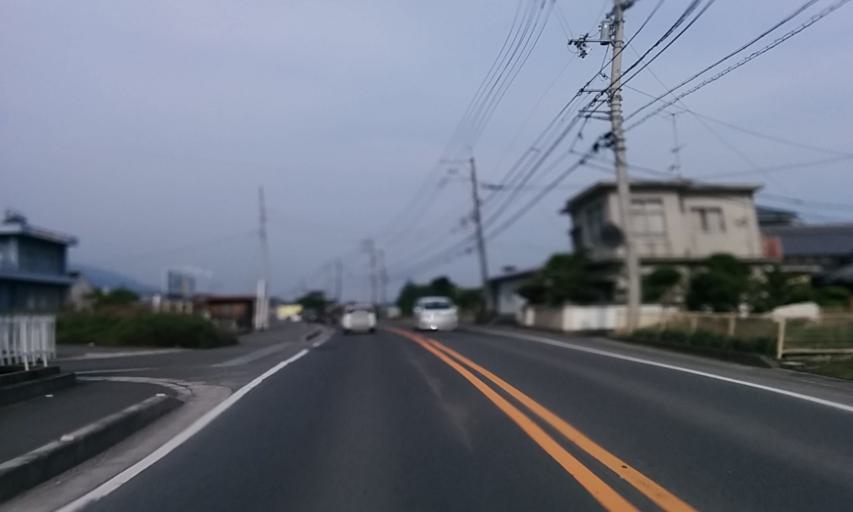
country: JP
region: Ehime
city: Kawanoecho
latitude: 33.9670
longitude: 133.4992
